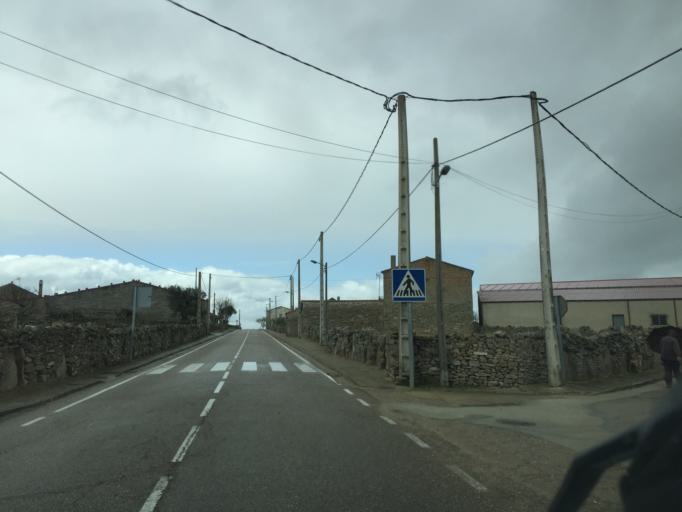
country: ES
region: Castille and Leon
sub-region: Provincia de Zamora
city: Villalcampo
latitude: 41.5212
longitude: -6.0508
